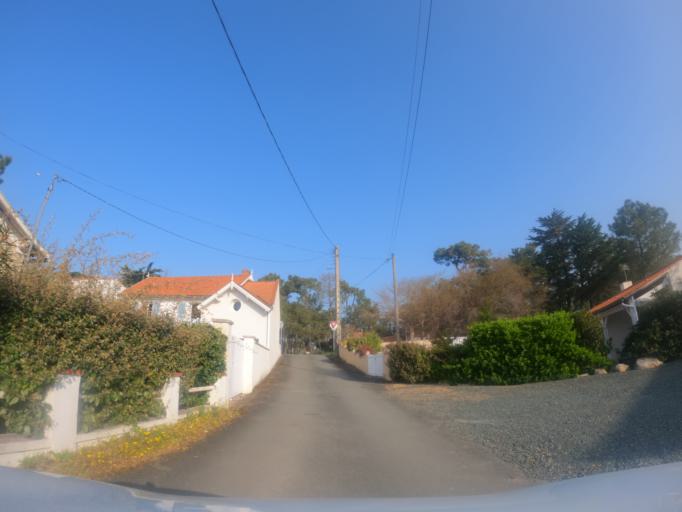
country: FR
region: Pays de la Loire
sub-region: Departement de la Vendee
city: La Tranche-sur-Mer
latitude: 46.3432
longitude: -1.4453
